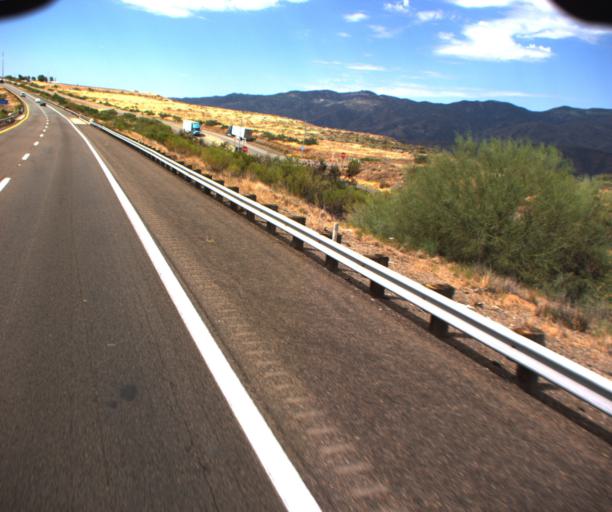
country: US
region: Arizona
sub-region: Yavapai County
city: Cordes Lakes
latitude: 34.1949
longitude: -112.1312
